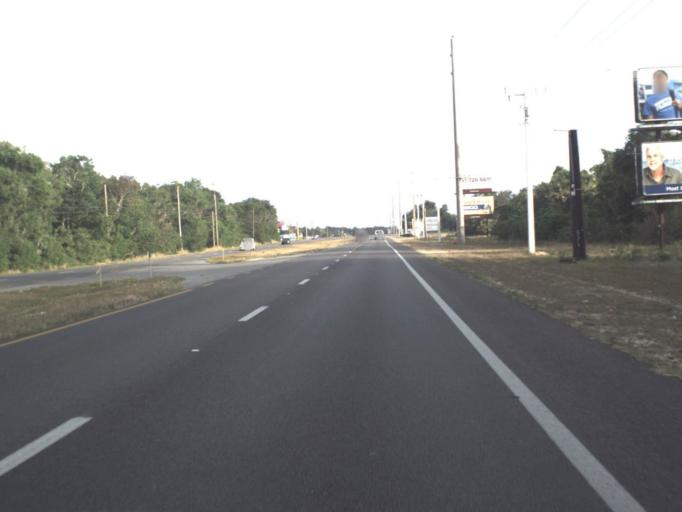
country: US
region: Florida
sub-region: Brevard County
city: Sharpes
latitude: 28.4253
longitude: -80.7581
